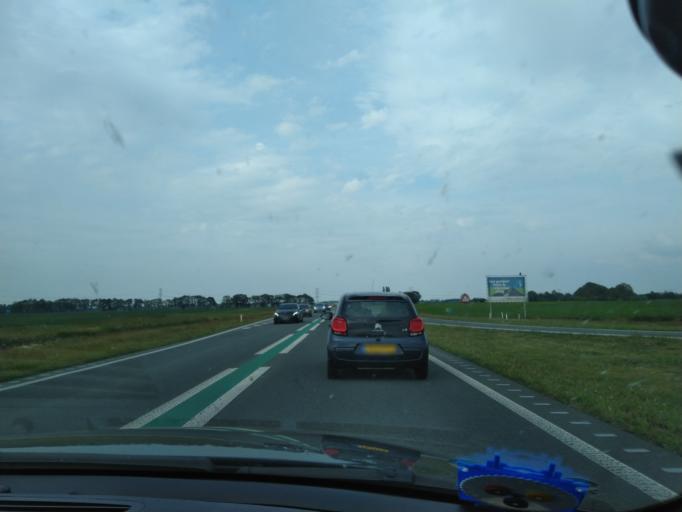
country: NL
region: Drenthe
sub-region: Gemeente Coevorden
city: Dalen
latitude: 52.7169
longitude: 6.7678
